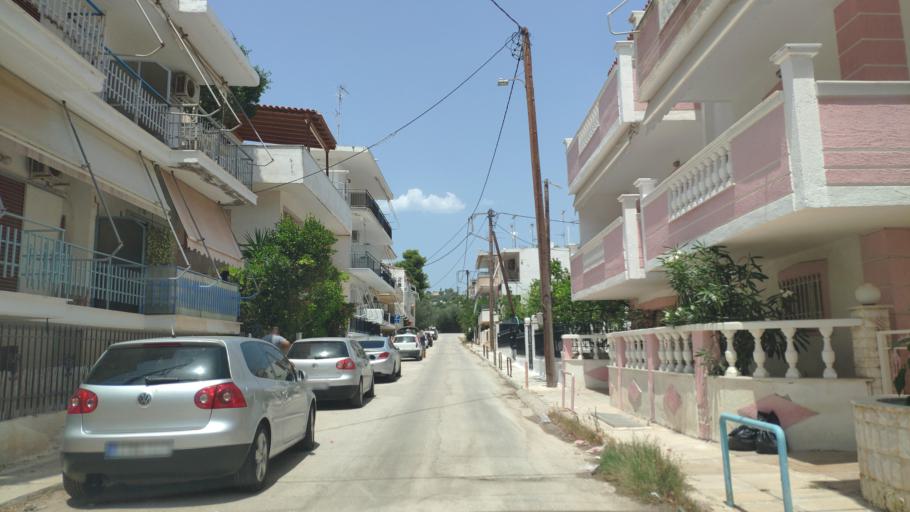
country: GR
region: Peloponnese
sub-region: Nomos Argolidos
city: Porto Cheli
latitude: 37.3281
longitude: 23.1482
